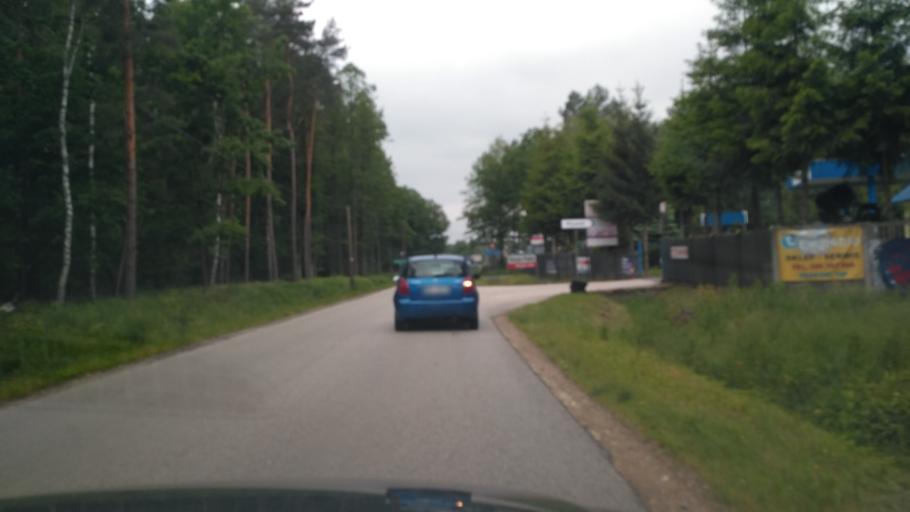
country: PL
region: Subcarpathian Voivodeship
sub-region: Powiat ropczycko-sedziszowski
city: Sedziszow Malopolski
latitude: 50.1316
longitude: 21.6706
